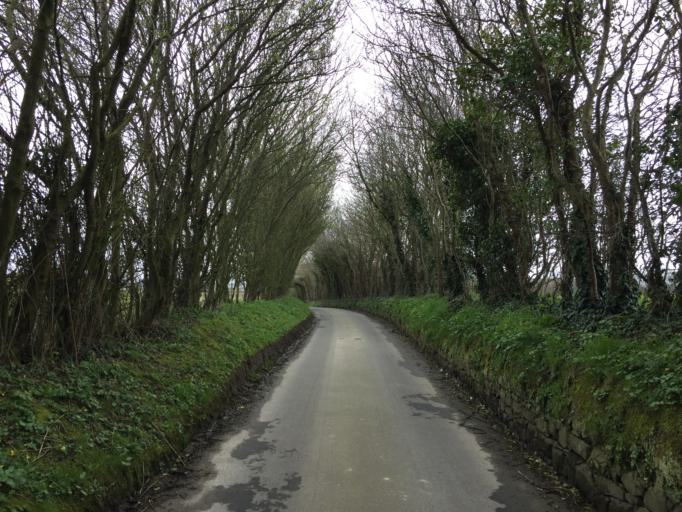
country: JE
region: St Helier
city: Saint Helier
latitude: 49.2041
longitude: -2.0621
